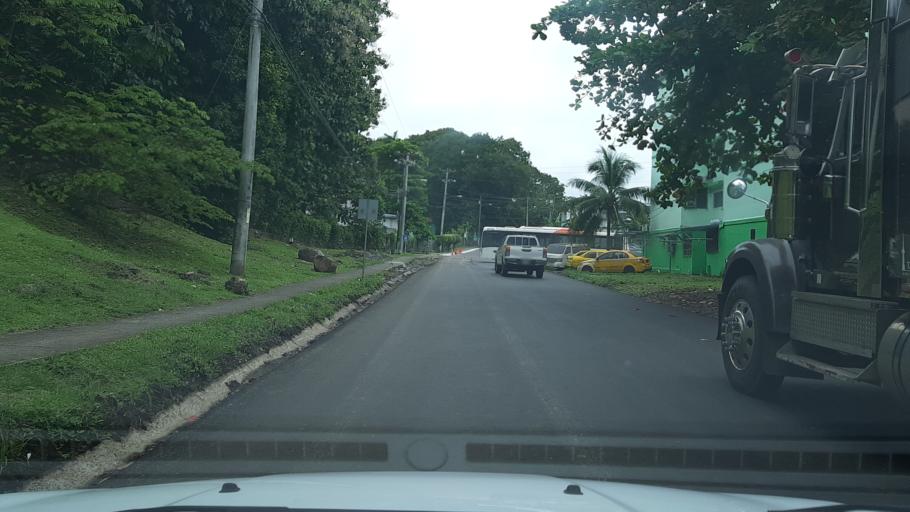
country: PA
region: Panama
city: San Miguelito
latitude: 9.0286
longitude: -79.4827
